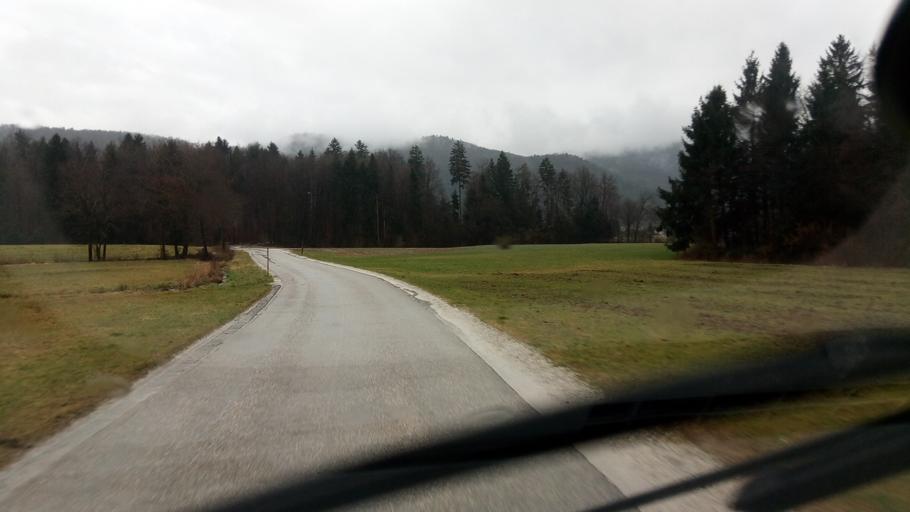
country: SI
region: Vodice
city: Vodice
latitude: 46.1673
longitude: 14.5152
